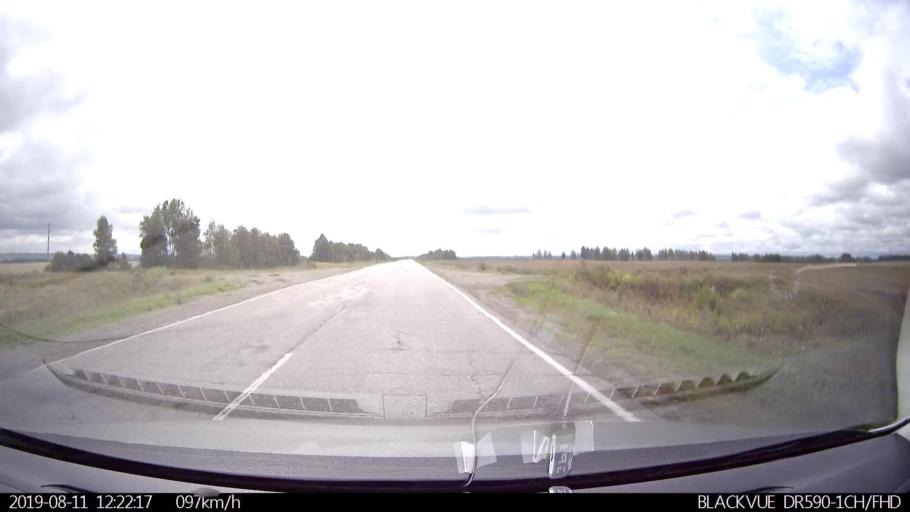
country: RU
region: Ulyanovsk
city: Ignatovka
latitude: 53.9099
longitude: 47.9547
